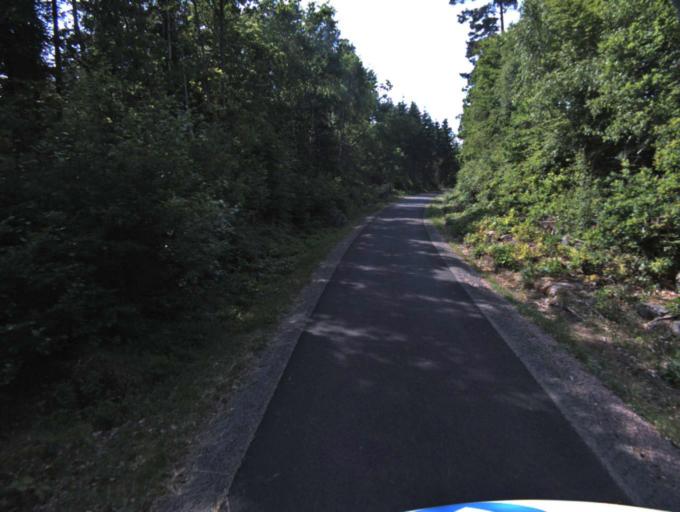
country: SE
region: Skane
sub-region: Kristianstads Kommun
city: Tollarp
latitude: 56.1961
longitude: 14.2622
